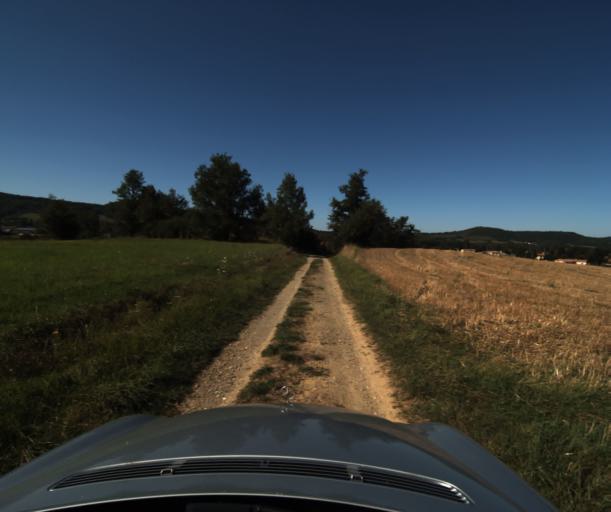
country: FR
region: Midi-Pyrenees
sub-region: Departement de l'Ariege
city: Lavelanet
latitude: 42.9829
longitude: 1.9112
